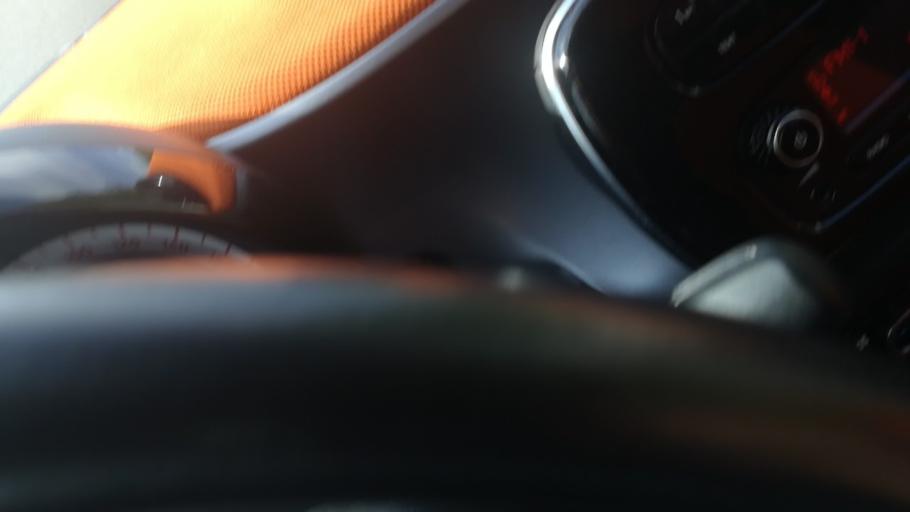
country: PT
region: Porto
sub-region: Valongo
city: Ermesinde
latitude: 41.2218
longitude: -8.5637
